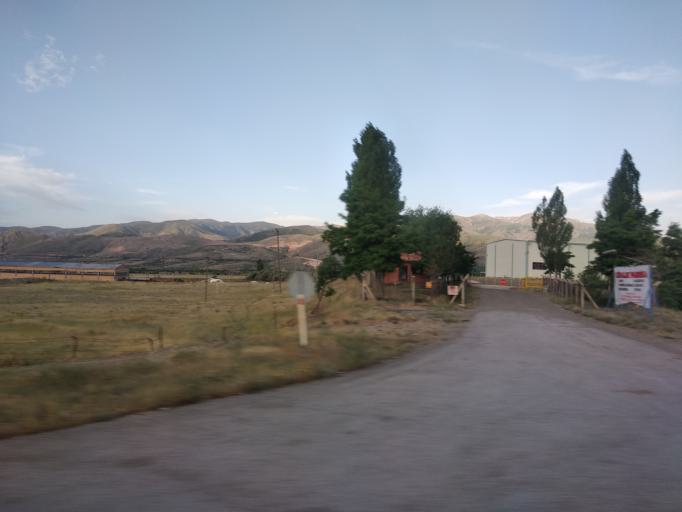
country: TR
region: Erzincan
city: Catalarmut
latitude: 39.8108
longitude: 39.3597
